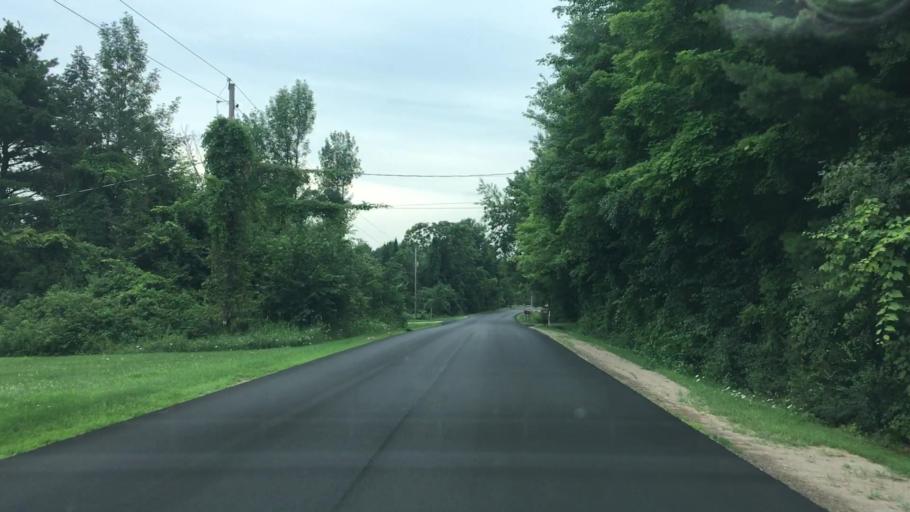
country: US
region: New York
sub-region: Clinton County
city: Peru
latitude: 44.5626
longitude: -73.5679
